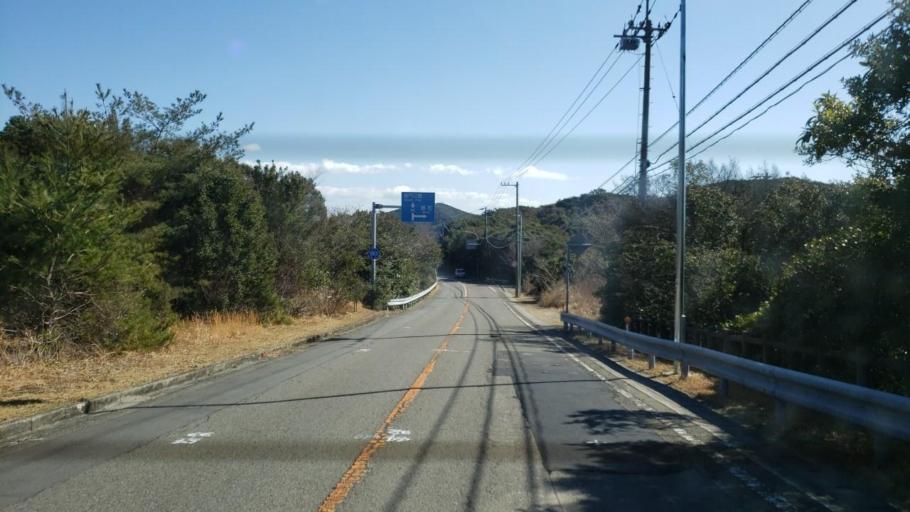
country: JP
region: Tokushima
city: Narutocho-mitsuishi
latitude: 34.2368
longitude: 134.6134
